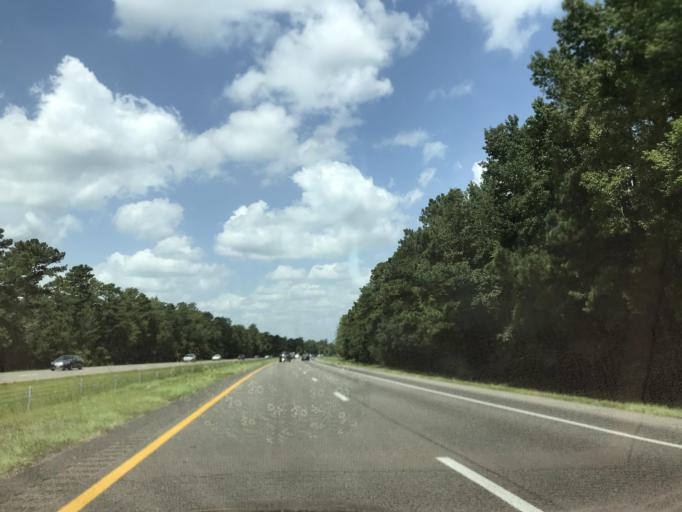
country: US
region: North Carolina
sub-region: Pender County
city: Burgaw
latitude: 34.6251
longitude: -77.9332
